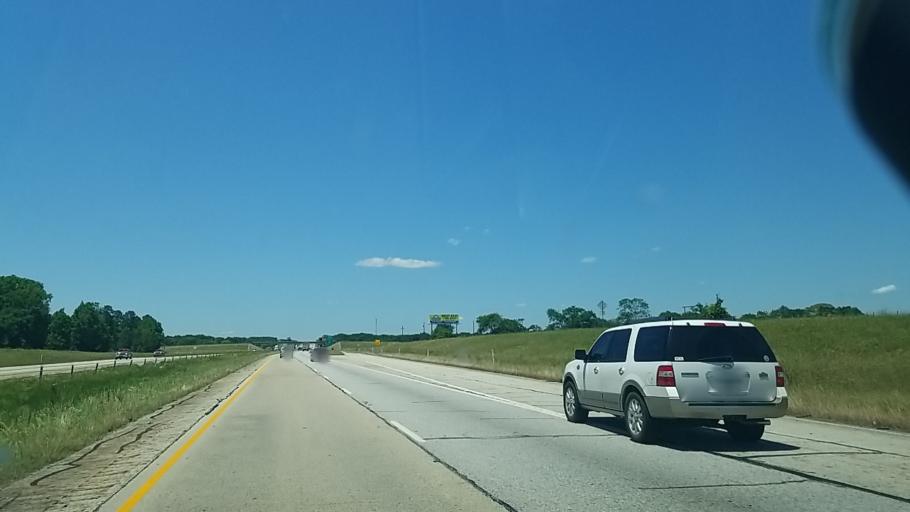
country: US
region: Texas
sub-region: Leon County
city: Centerville
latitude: 31.1442
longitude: -95.9817
